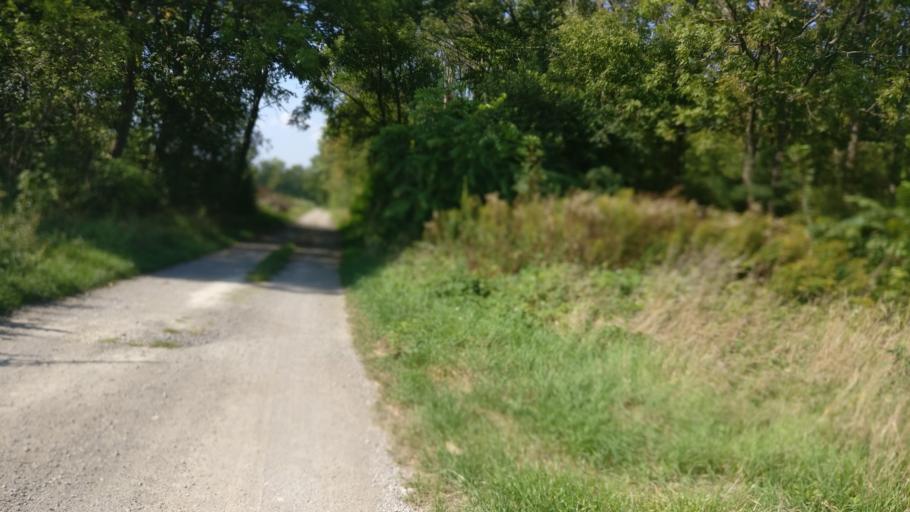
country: AT
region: Lower Austria
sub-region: Politischer Bezirk Wien-Umgebung
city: Moosbrunn
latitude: 47.9938
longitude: 16.4140
